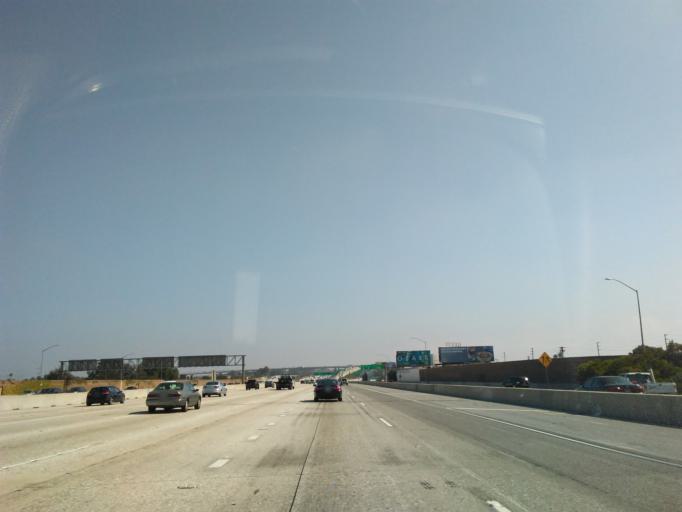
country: US
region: California
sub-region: Los Angeles County
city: Lennox
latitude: 33.9432
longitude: -118.3686
